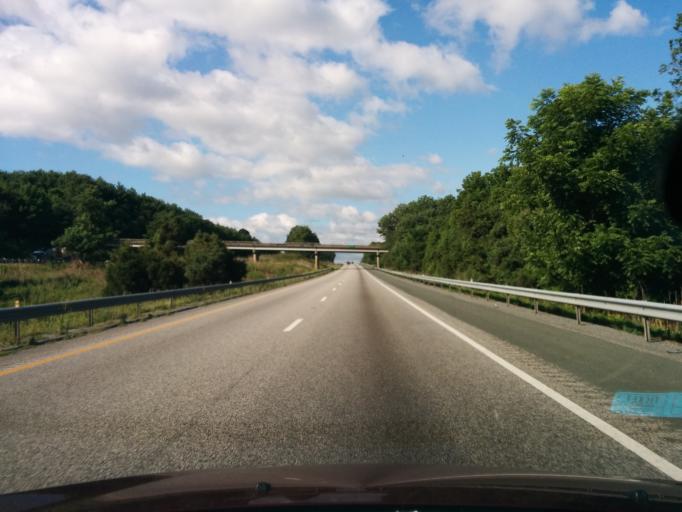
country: US
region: Virginia
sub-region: City of Lexington
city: Lexington
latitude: 37.7420
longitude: -79.4219
